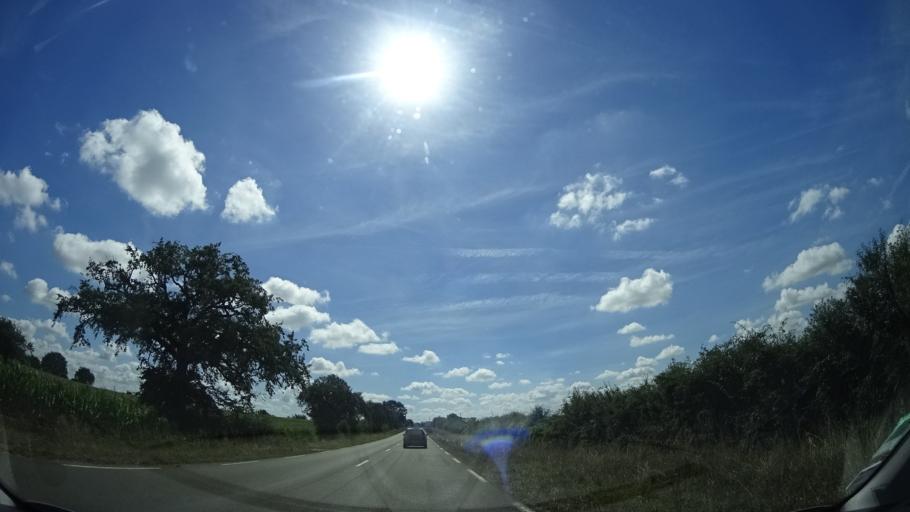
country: FR
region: Pays de la Loire
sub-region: Departement de la Sarthe
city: Auvers-le-Hamon
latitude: 47.8950
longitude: -0.4279
